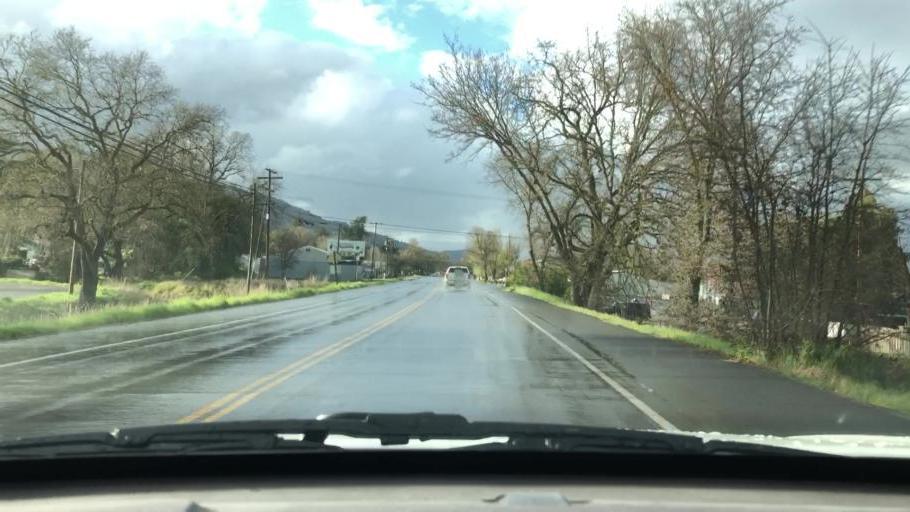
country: US
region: California
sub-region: Mendocino County
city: Ukiah
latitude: 39.1176
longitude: -123.2005
